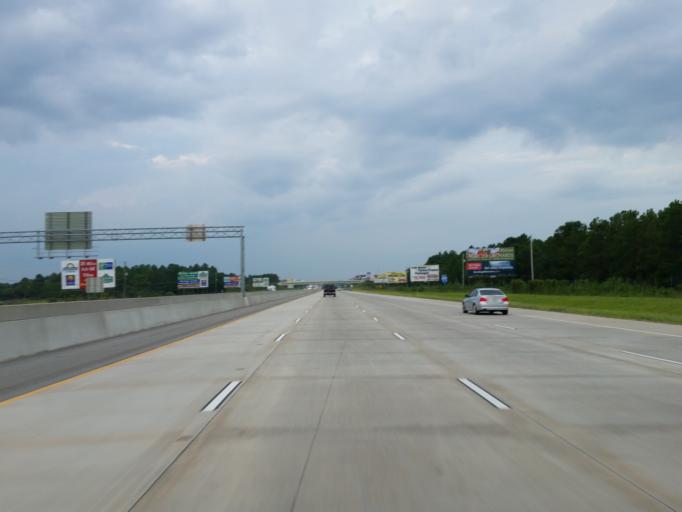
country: US
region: Georgia
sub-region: Cook County
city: Adel
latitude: 31.1412
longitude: -83.4407
